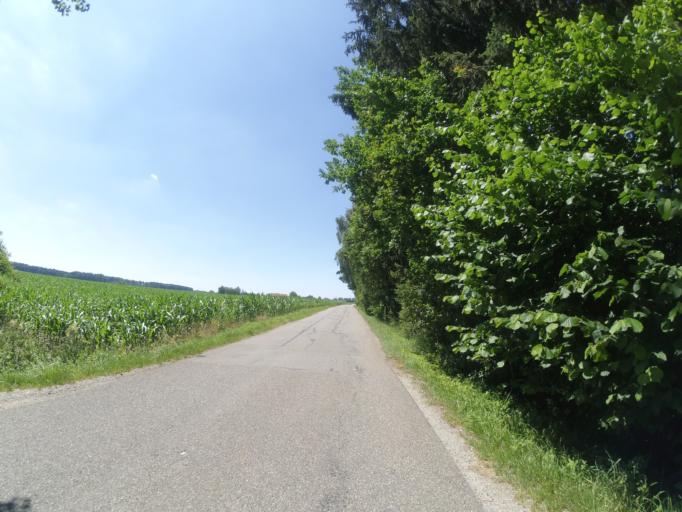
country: DE
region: Baden-Wuerttemberg
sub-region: Tuebingen Region
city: Bad Waldsee
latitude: 47.9218
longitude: 9.7080
